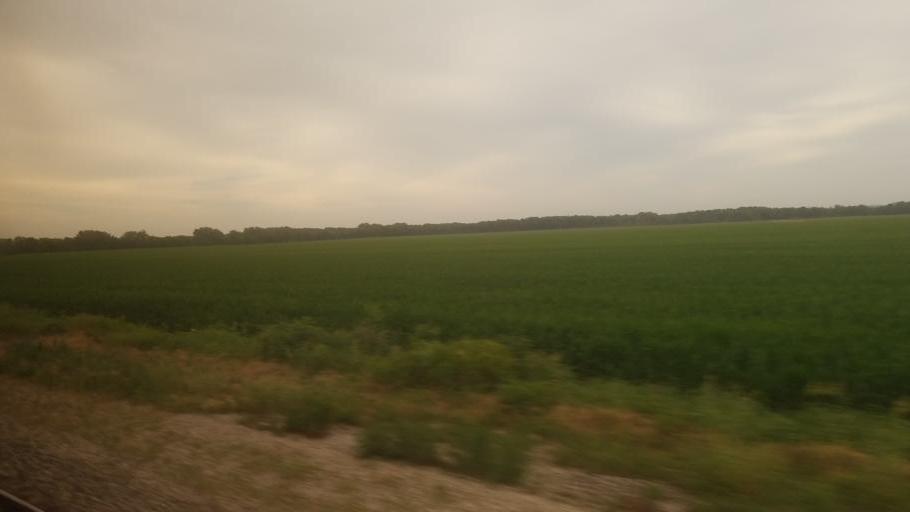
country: US
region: Kansas
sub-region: Chase County
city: Cottonwood Falls
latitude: 38.3900
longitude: -96.5263
